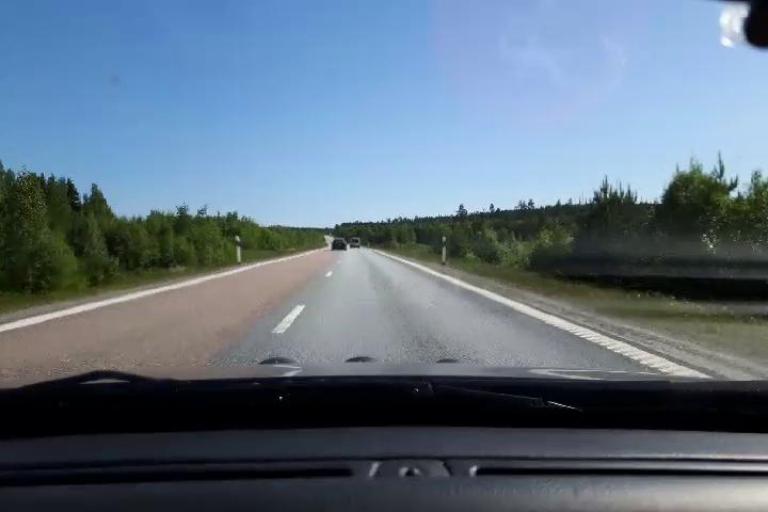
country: SE
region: Gaevleborg
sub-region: Hudiksvalls Kommun
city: Iggesund
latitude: 61.4839
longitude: 16.9848
